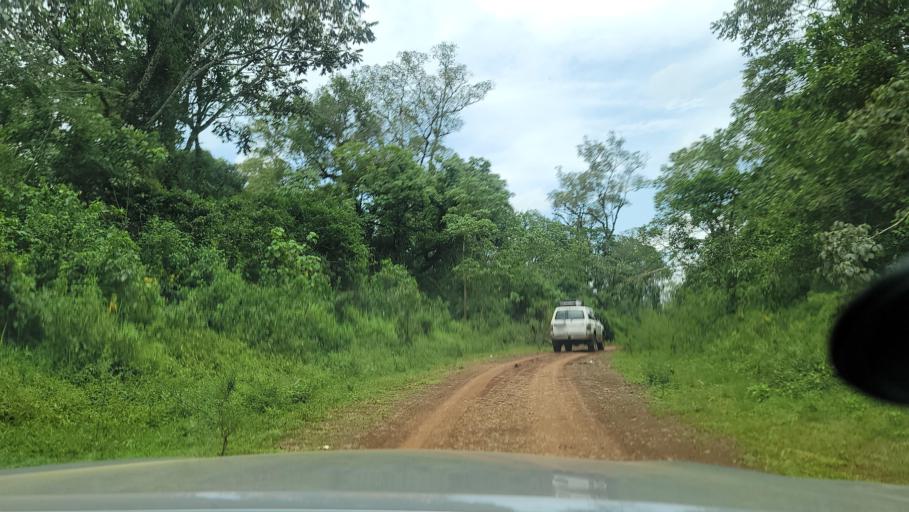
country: ET
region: Southern Nations, Nationalities, and People's Region
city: Bonga
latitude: 7.6447
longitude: 36.2435
